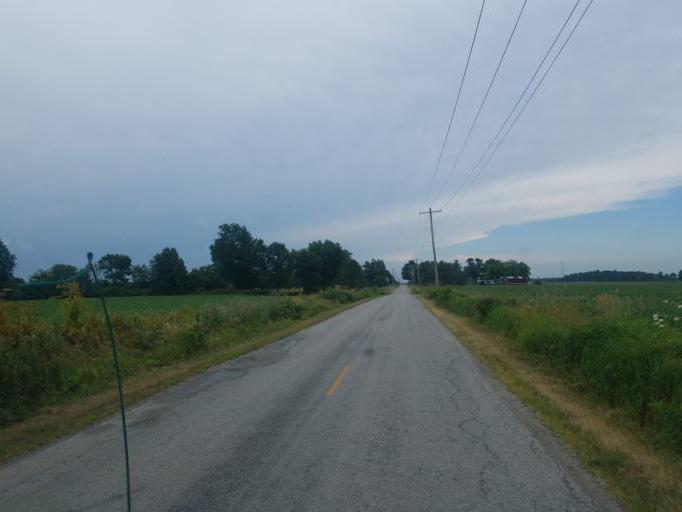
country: US
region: Indiana
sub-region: DeKalb County
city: Butler
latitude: 41.3759
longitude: -84.8887
